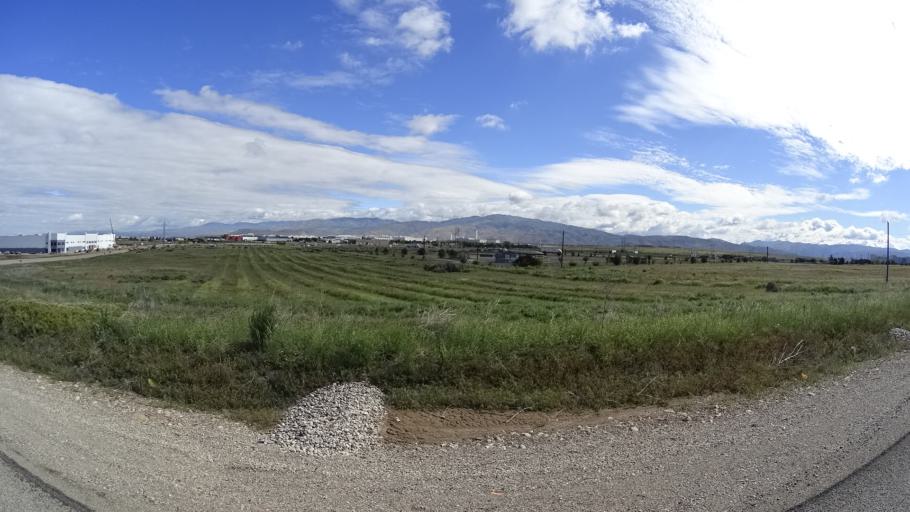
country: US
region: Idaho
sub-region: Ada County
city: Boise
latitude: 43.5117
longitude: -116.1501
